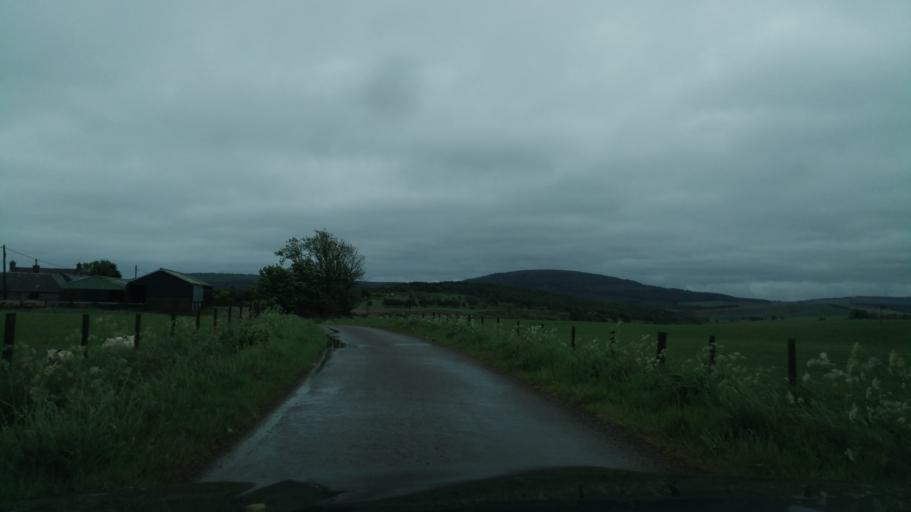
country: GB
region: Scotland
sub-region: Moray
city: Keith
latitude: 57.5731
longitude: -2.8612
